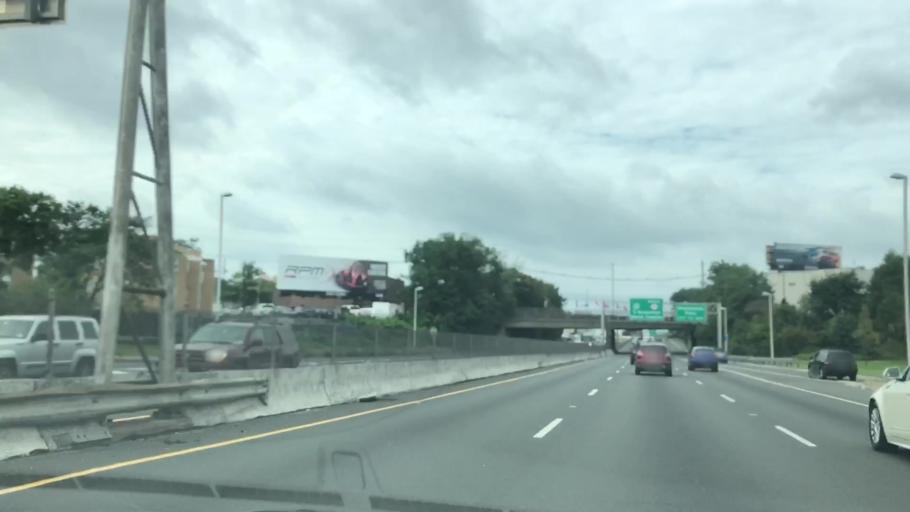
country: US
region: New Jersey
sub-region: Hudson County
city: Secaucus
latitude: 40.7933
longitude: -74.0568
